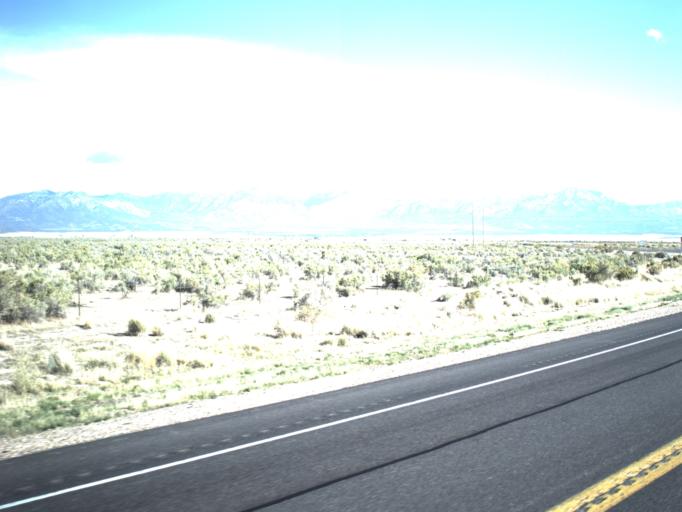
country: US
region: Utah
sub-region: Millard County
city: Fillmore
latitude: 39.1573
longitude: -112.4096
